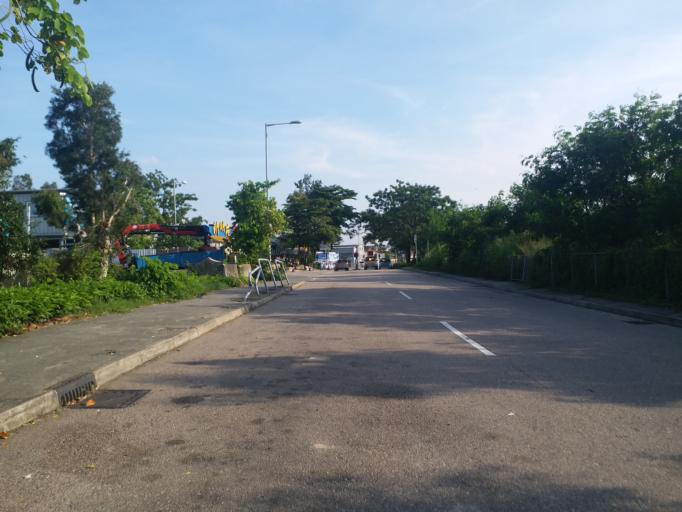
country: HK
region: Yuen Long
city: Yuen Long Kau Hui
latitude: 22.4739
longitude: 114.0514
